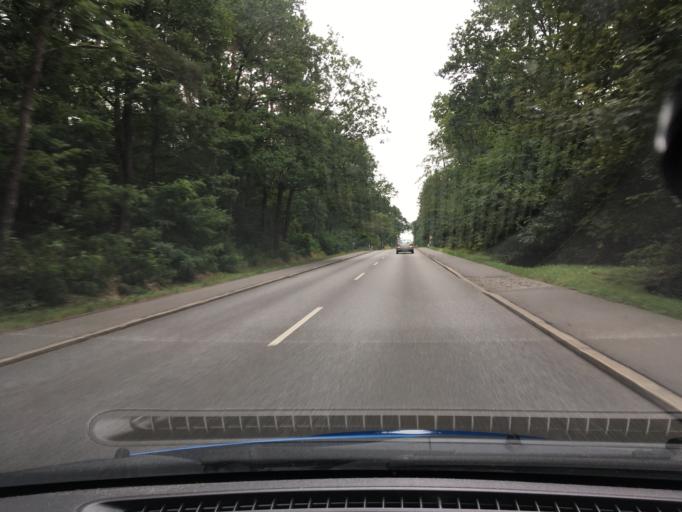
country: DE
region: Schleswig-Holstein
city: Geesthacht
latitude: 53.4303
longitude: 10.3936
